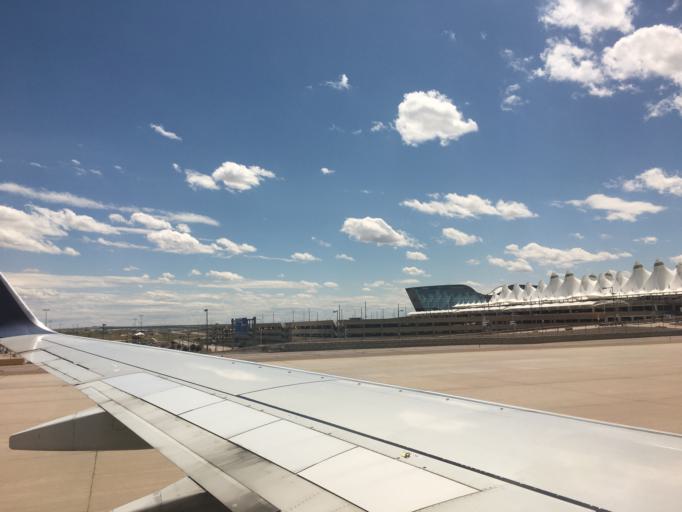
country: US
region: Colorado
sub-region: Weld County
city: Lochbuie
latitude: 39.8528
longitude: -104.6690
